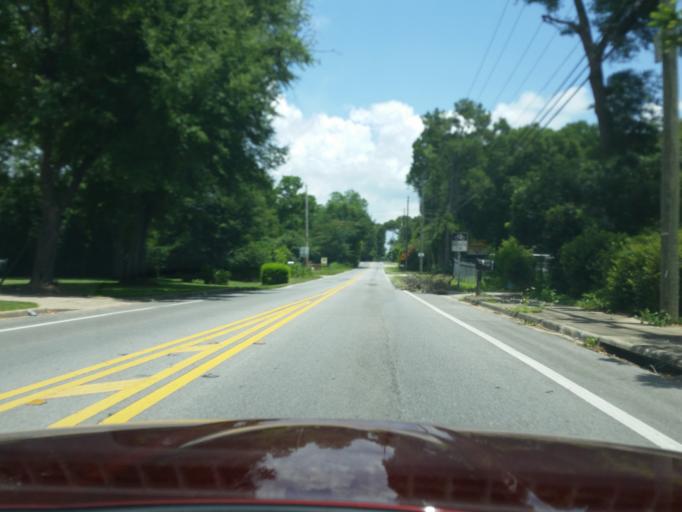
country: US
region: Florida
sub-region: Escambia County
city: Ensley
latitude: 30.5479
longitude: -87.2799
